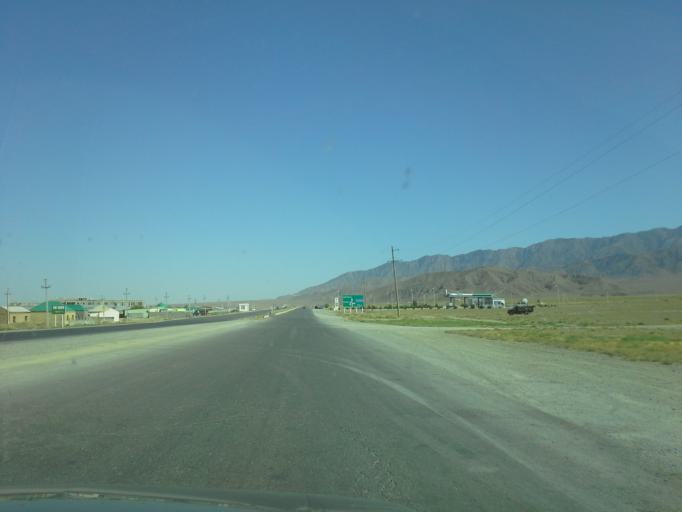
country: TM
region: Ahal
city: Baharly
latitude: 38.5411
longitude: 57.1518
